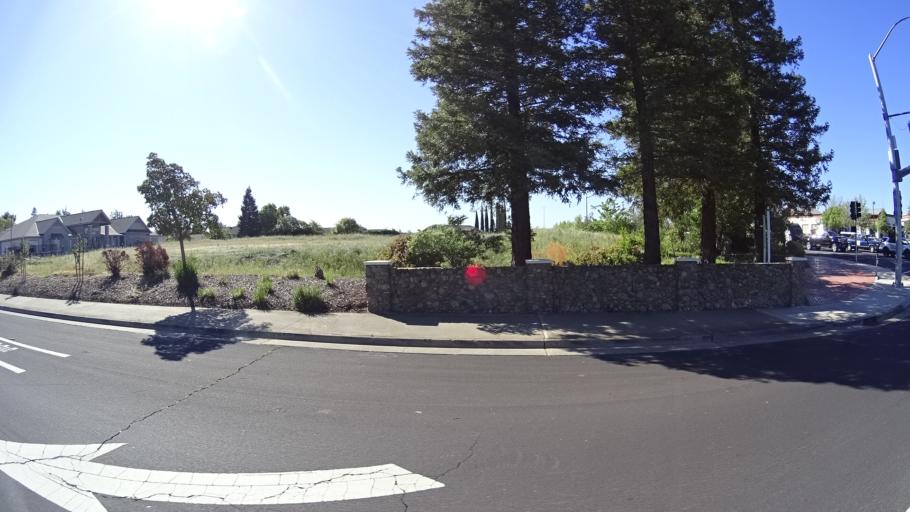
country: US
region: California
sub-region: Placer County
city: Rocklin
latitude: 38.7963
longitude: -121.2647
